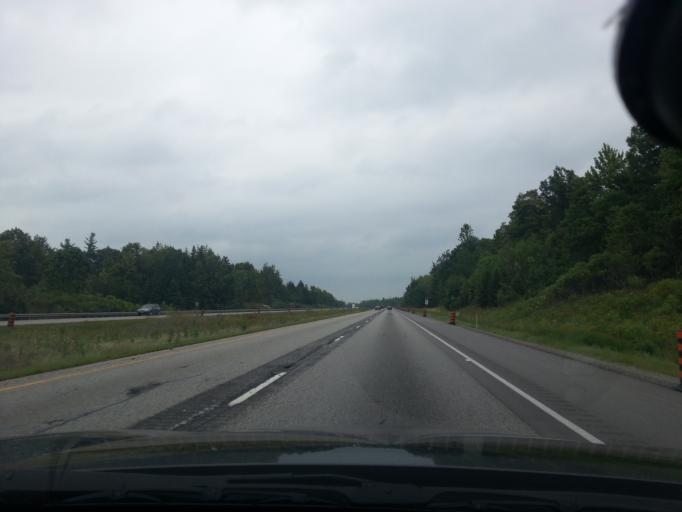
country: US
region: New York
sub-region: Jefferson County
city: Alexandria Bay
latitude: 44.4214
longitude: -75.9104
